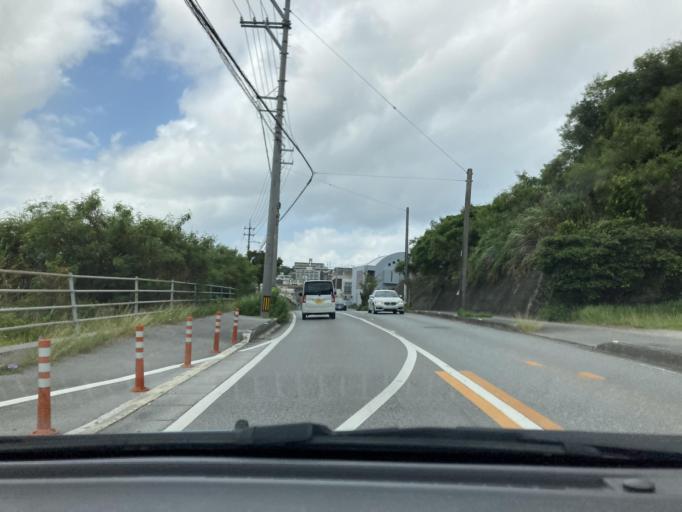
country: JP
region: Okinawa
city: Ginowan
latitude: 26.2409
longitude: 127.7560
